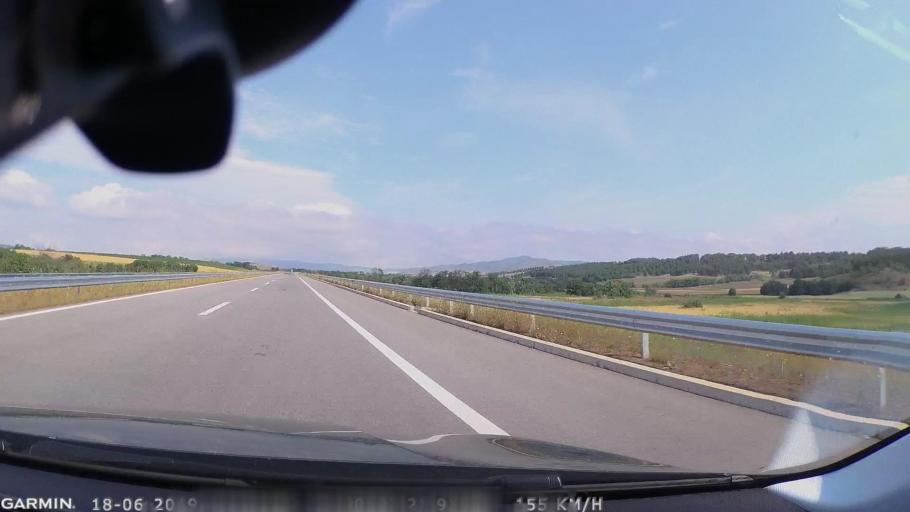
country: MK
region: Sveti Nikole
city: Gorobinci
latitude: 41.9051
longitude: 21.9094
